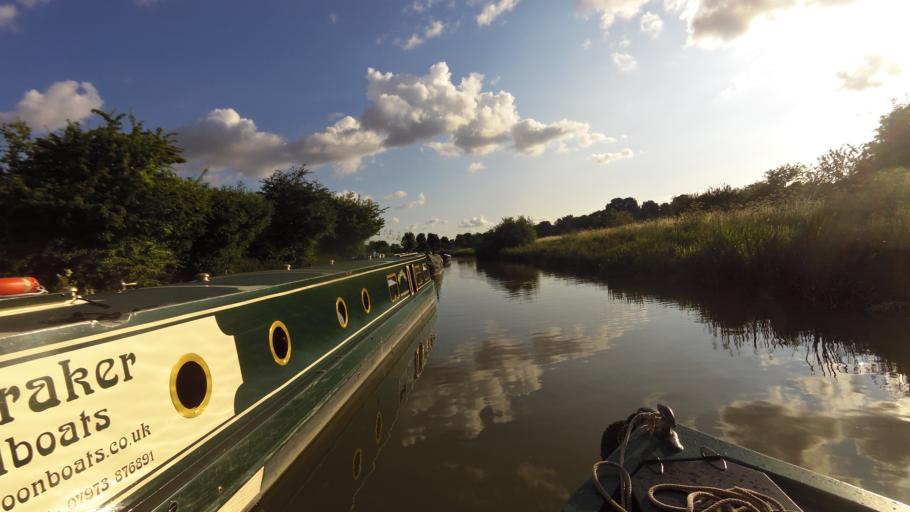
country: GB
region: England
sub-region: Wiltshire
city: Great Bedwyn
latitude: 51.3820
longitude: -1.5949
